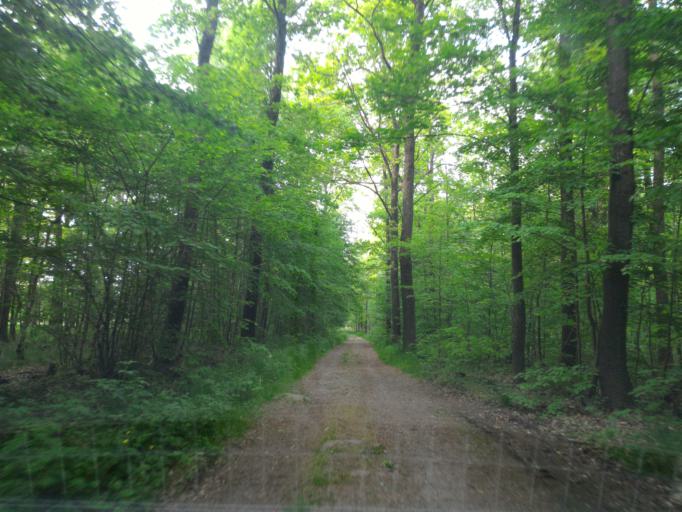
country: DE
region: Saxony
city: Grossschonau
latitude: 50.8731
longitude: 14.6649
